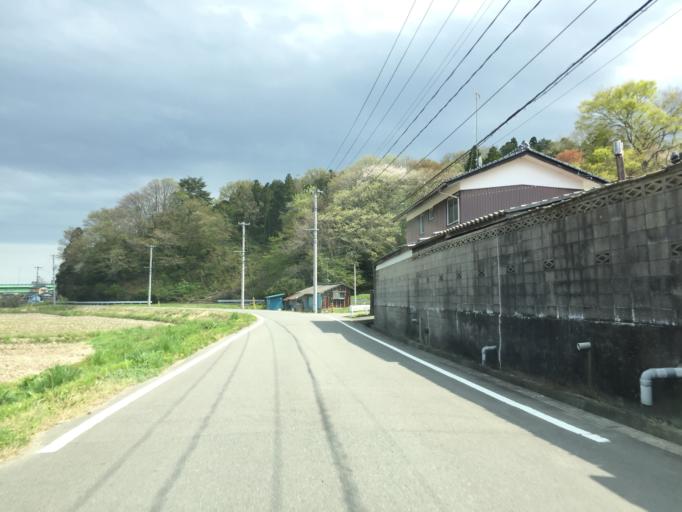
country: JP
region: Fukushima
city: Iwaki
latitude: 37.1500
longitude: 140.9858
